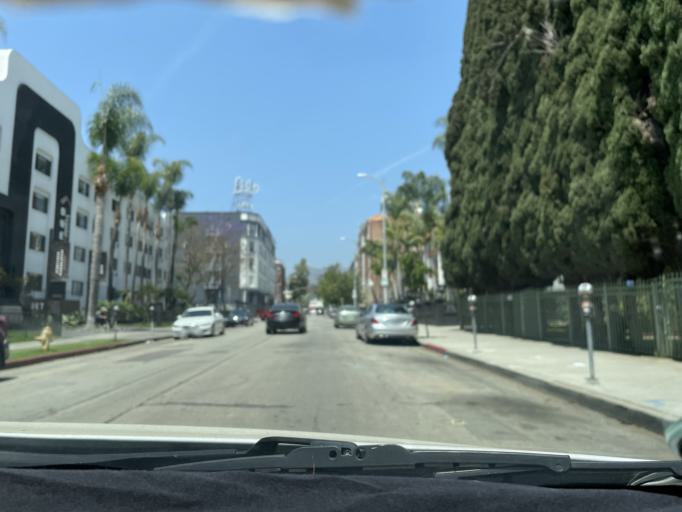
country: US
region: California
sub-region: Los Angeles County
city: Hollywood
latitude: 34.1027
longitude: -118.3310
